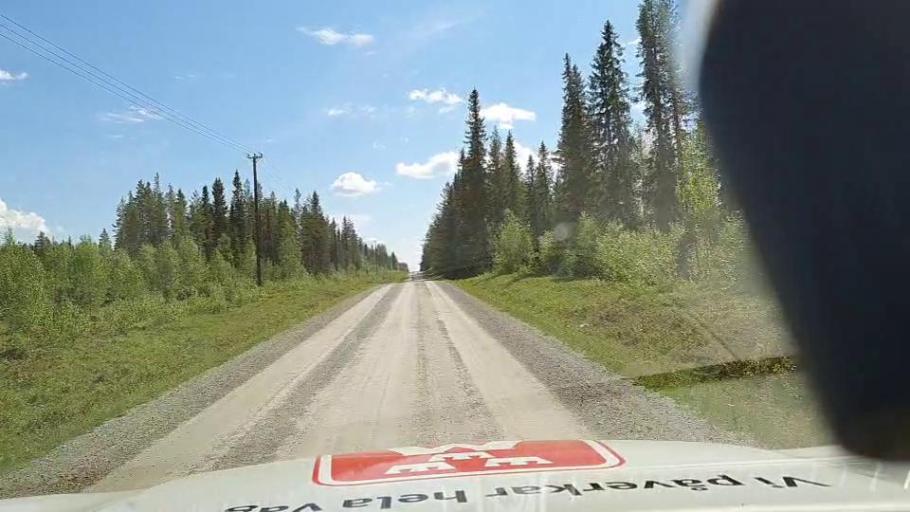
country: SE
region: Jaemtland
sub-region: Stroemsunds Kommun
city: Stroemsund
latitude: 64.4837
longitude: 15.5919
